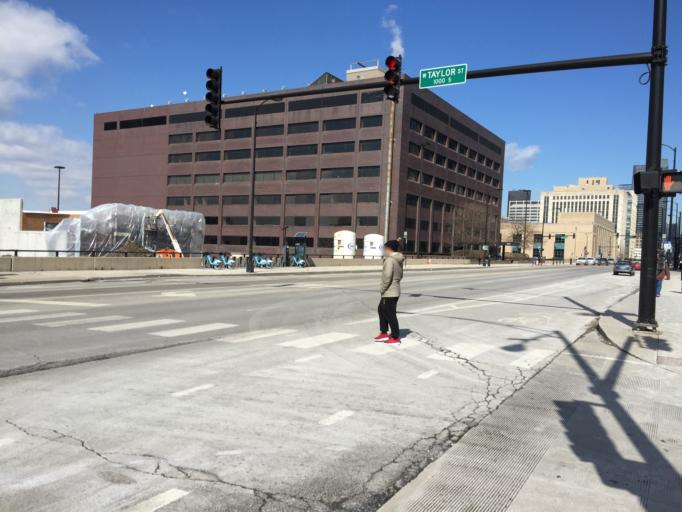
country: US
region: Illinois
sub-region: Cook County
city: Chicago
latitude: 41.8699
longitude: -87.6392
